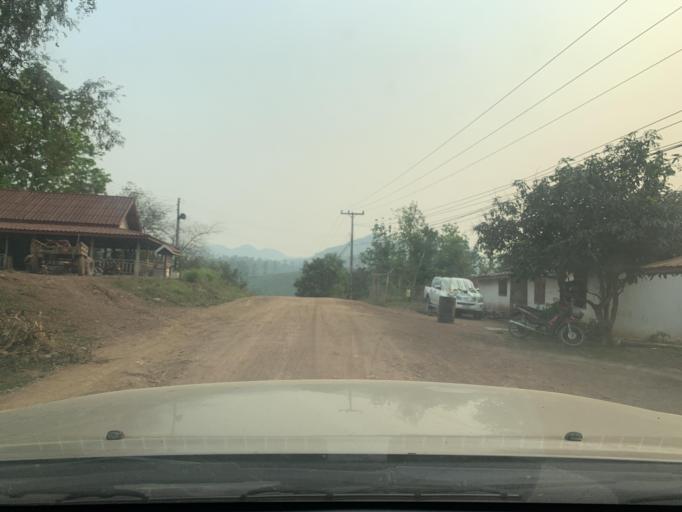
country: LA
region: Louangphabang
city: Louangphabang
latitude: 19.9181
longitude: 102.0750
